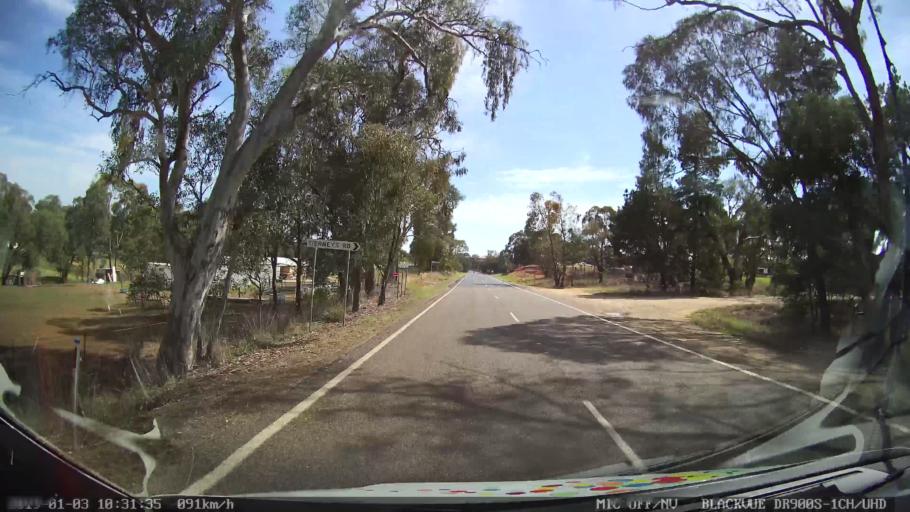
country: AU
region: New South Wales
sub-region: Young
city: Young
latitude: -34.3485
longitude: 148.2787
